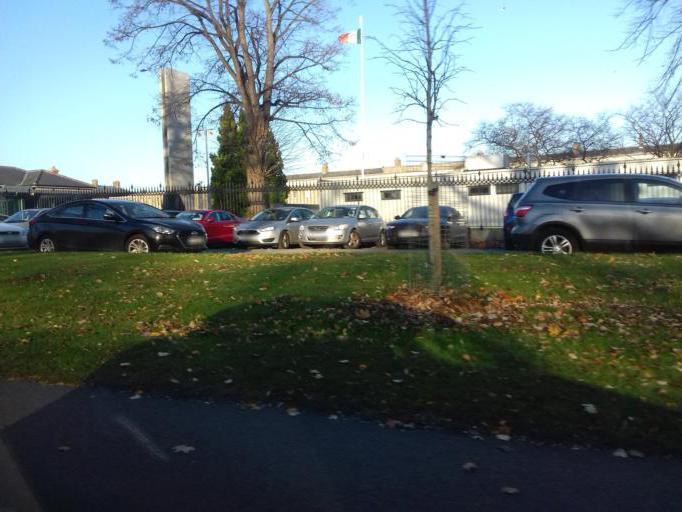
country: IE
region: Leinster
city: Cabra
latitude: 53.3533
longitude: -6.3016
